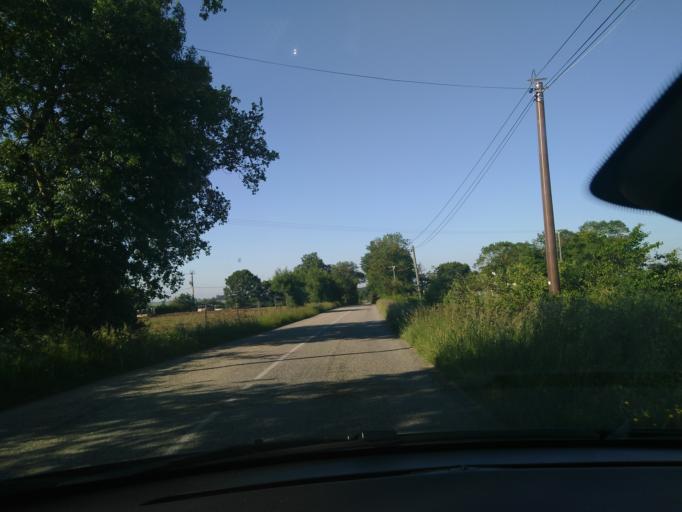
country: FR
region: Midi-Pyrenees
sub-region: Departement du Gers
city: Gimont
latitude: 43.7019
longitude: 0.8792
